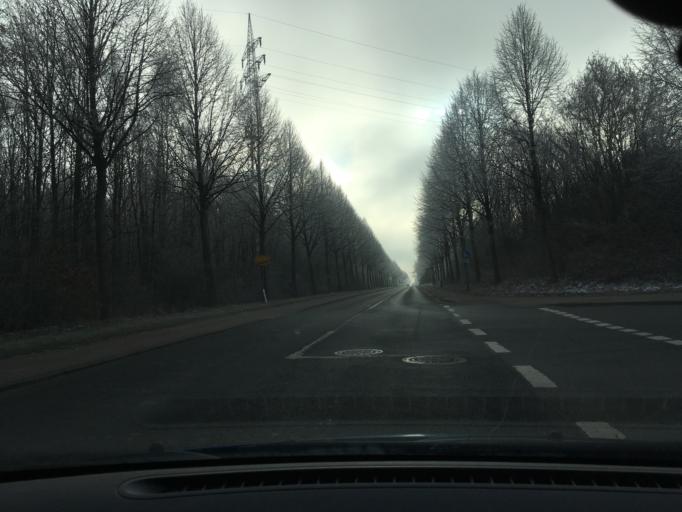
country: DE
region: Lower Saxony
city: Bardowick
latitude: 53.2697
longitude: 10.3888
